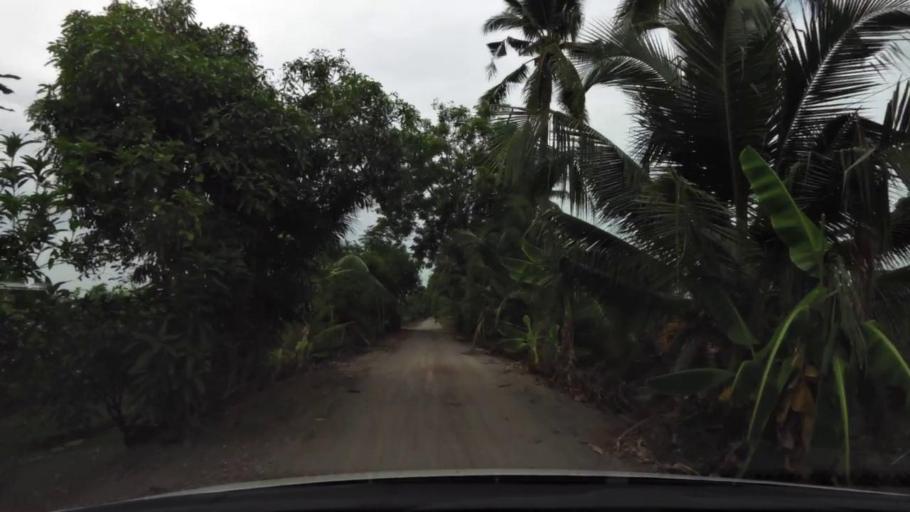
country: TH
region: Ratchaburi
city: Damnoen Saduak
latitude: 13.5668
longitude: 100.0031
